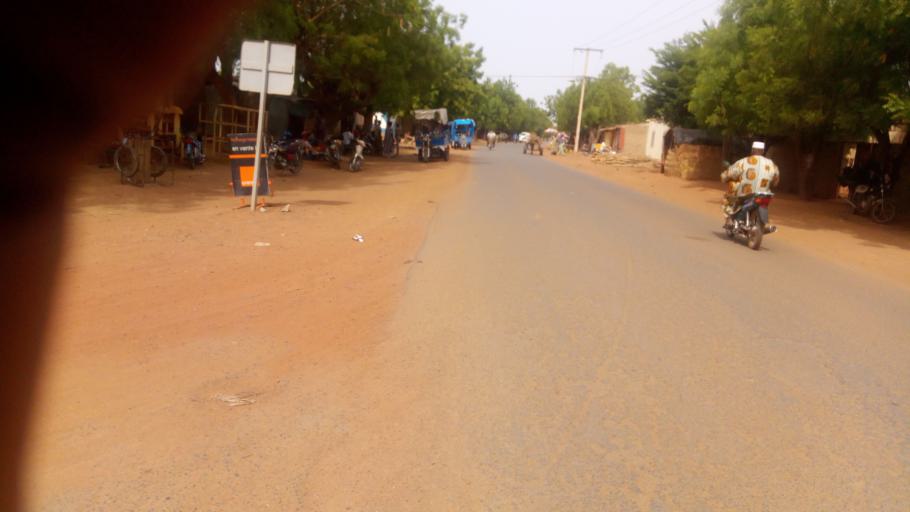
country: ML
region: Segou
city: Segou
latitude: 13.4347
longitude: -6.2899
